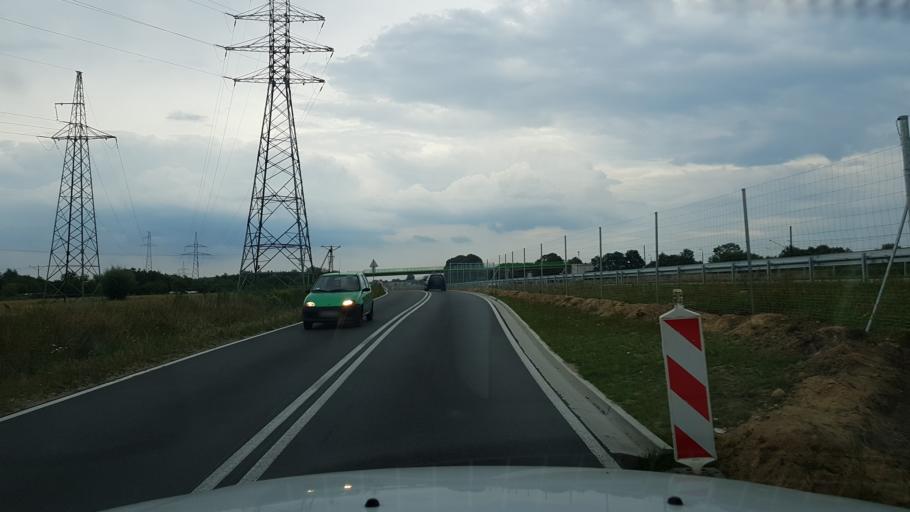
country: PL
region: West Pomeranian Voivodeship
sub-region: Powiat szczecinecki
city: Szczecinek
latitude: 53.7204
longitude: 16.6936
